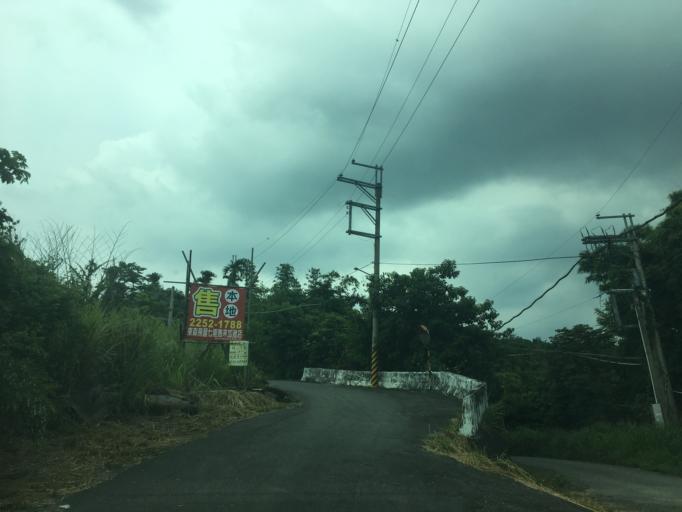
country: TW
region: Taiwan
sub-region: Taichung City
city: Taichung
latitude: 24.1676
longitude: 120.7572
